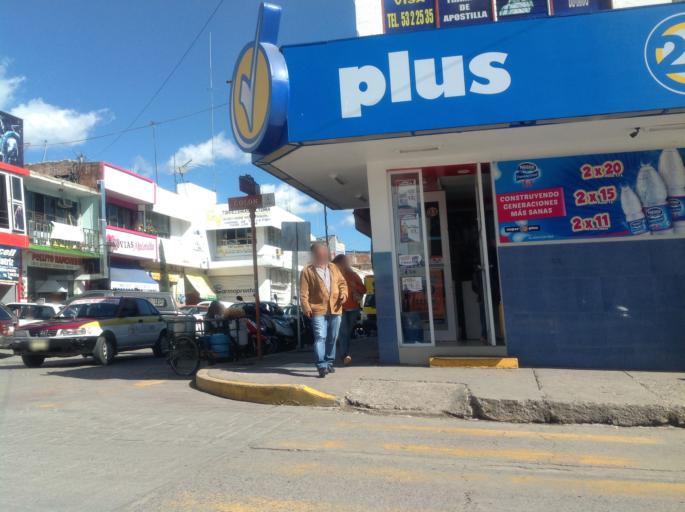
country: MX
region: Oaxaca
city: Ciudad de Huajuapam de Leon
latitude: 17.8078
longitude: -97.7759
